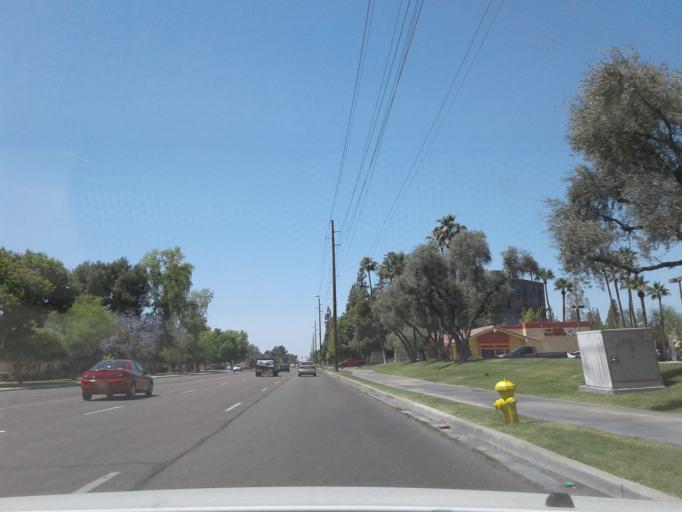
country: US
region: Arizona
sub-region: Maricopa County
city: Tempe
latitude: 33.3930
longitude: -111.9125
